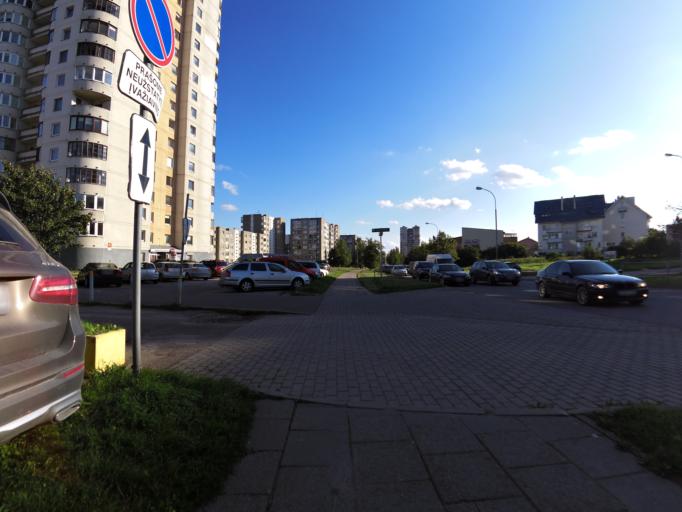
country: LT
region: Vilnius County
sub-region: Vilnius
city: Fabijoniskes
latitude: 54.7298
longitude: 25.2457
